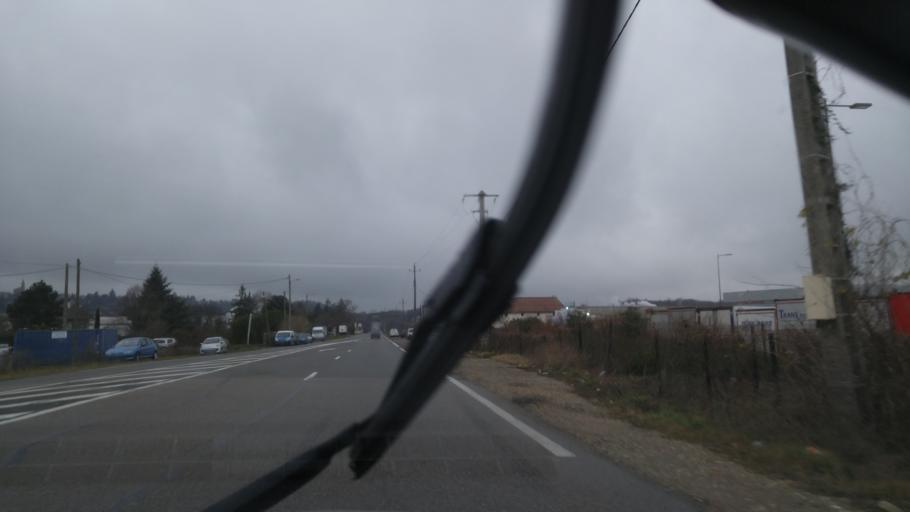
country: FR
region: Rhone-Alpes
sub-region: Departement de l'Isere
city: Grenay
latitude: 45.6614
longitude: 5.1007
